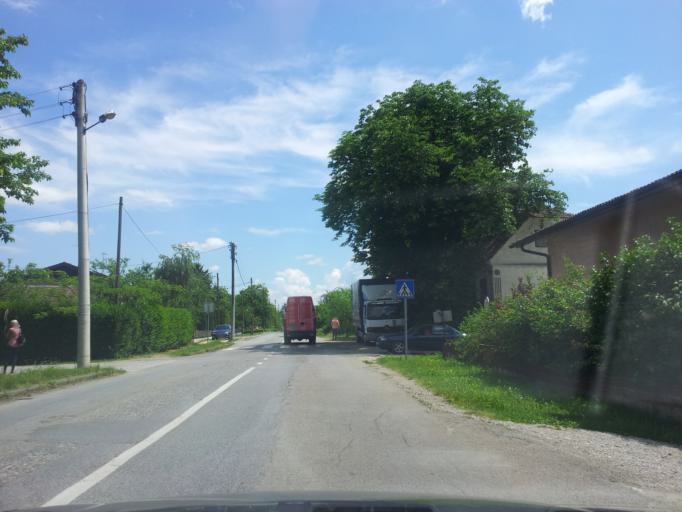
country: HR
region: Grad Zagreb
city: Lucko
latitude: 45.7563
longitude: 15.8451
